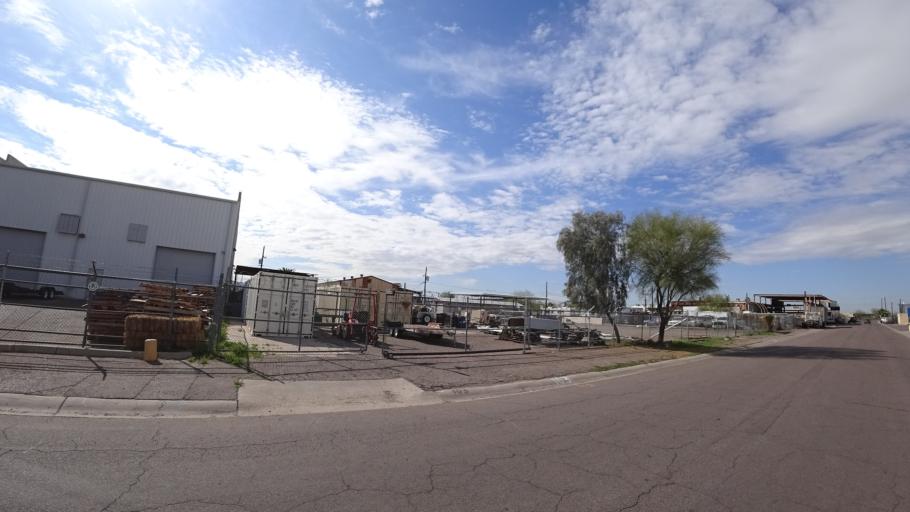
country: US
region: Arizona
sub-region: Maricopa County
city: Phoenix
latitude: 33.4175
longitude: -112.0709
